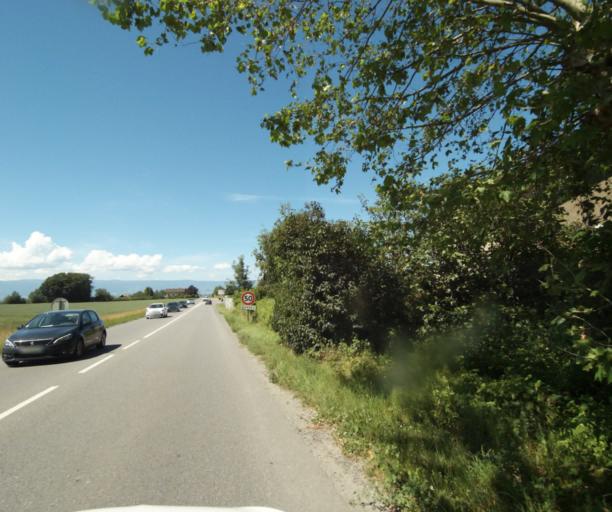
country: FR
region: Rhone-Alpes
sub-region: Departement de la Haute-Savoie
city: Loisin
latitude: 46.2739
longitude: 6.3127
